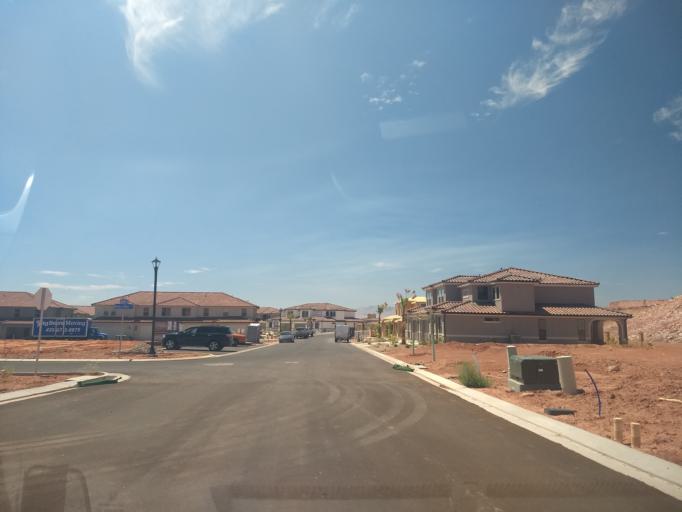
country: US
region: Utah
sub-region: Washington County
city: Washington
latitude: 37.1474
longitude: -113.4713
